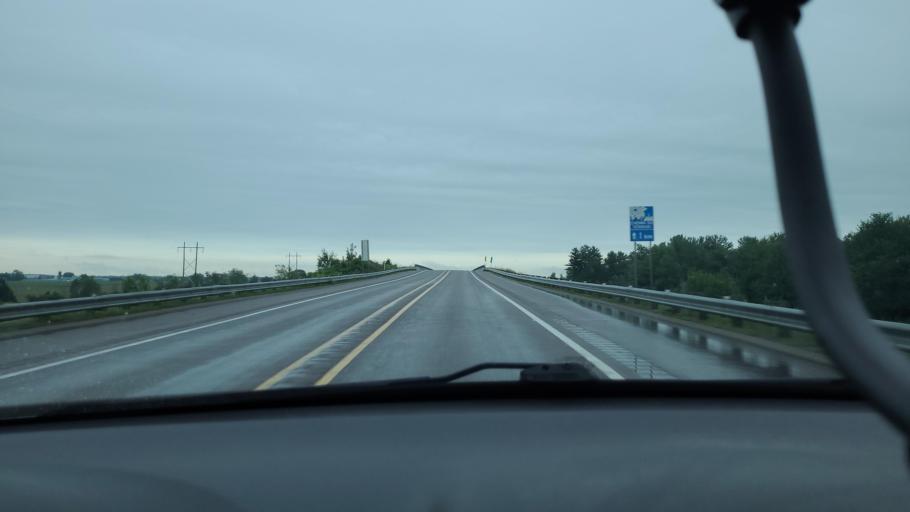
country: CA
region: Quebec
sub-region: Laurentides
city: Brownsburg-Chatham
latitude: 45.6373
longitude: -74.4428
